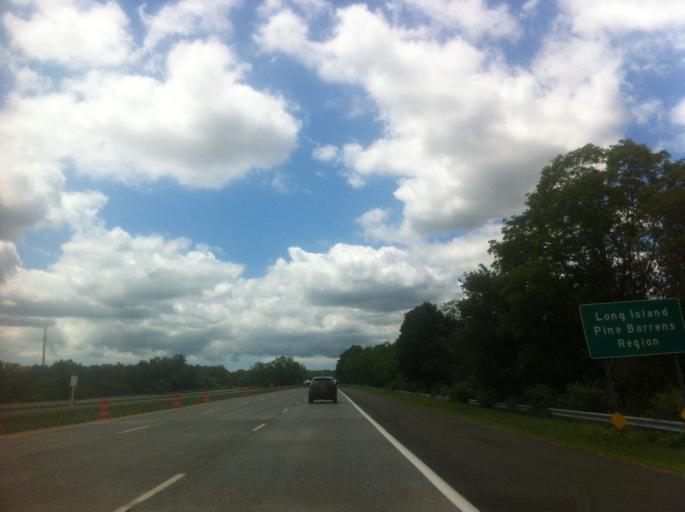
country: US
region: New York
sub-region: Suffolk County
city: Calverton
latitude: 40.9060
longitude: -72.7395
